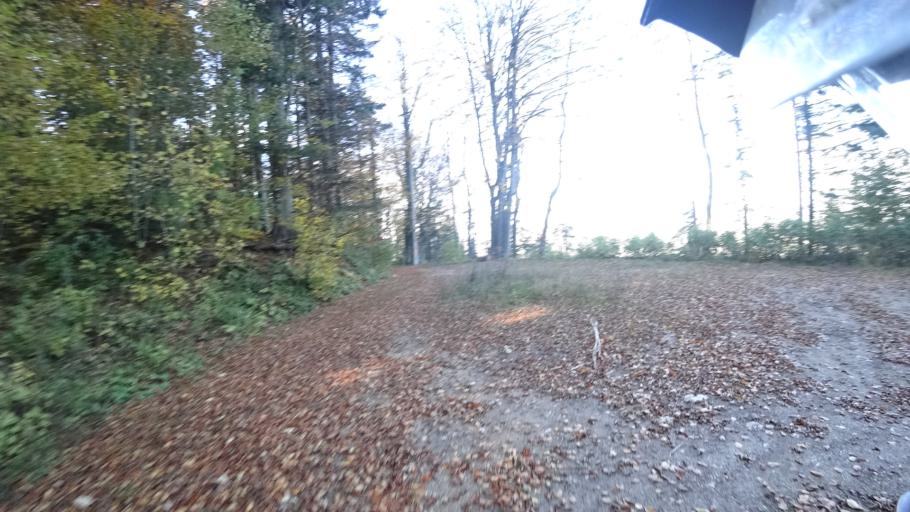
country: HR
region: Karlovacka
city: Plaski
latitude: 45.0008
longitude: 15.3982
